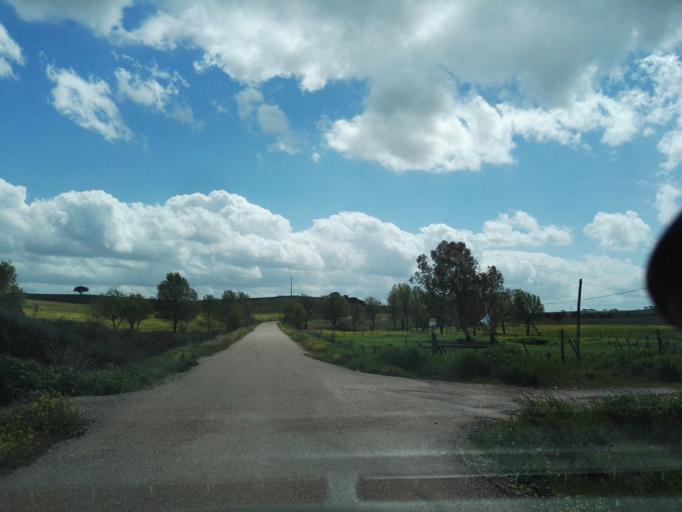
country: PT
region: Portalegre
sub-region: Elvas
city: Elvas
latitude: 38.9723
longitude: -7.1733
